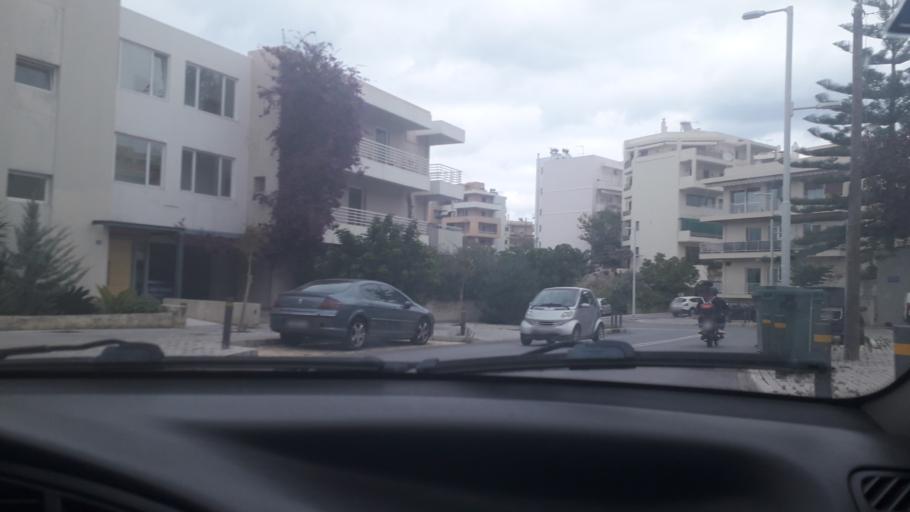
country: GR
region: Crete
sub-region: Nomos Rethymnis
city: Rethymno
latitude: 35.3590
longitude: 24.4750
